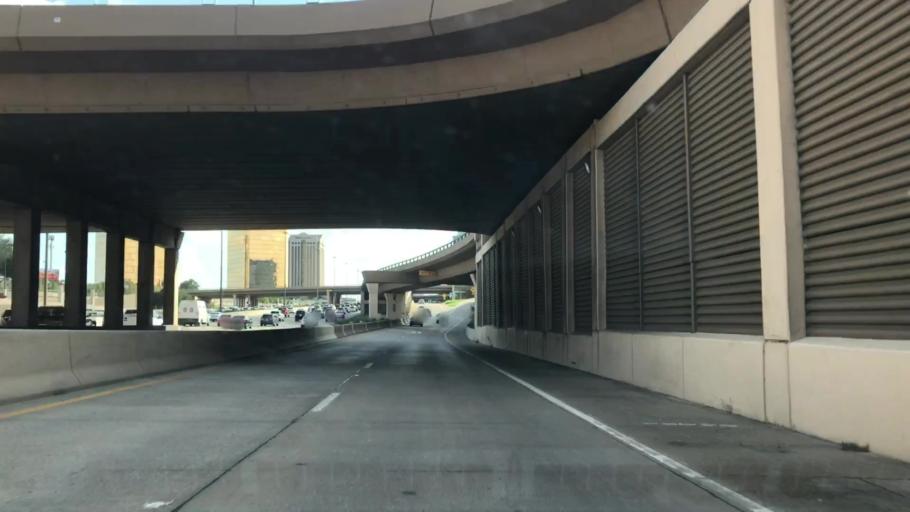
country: US
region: Texas
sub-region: Dallas County
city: University Park
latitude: 32.8688
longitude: -96.7707
